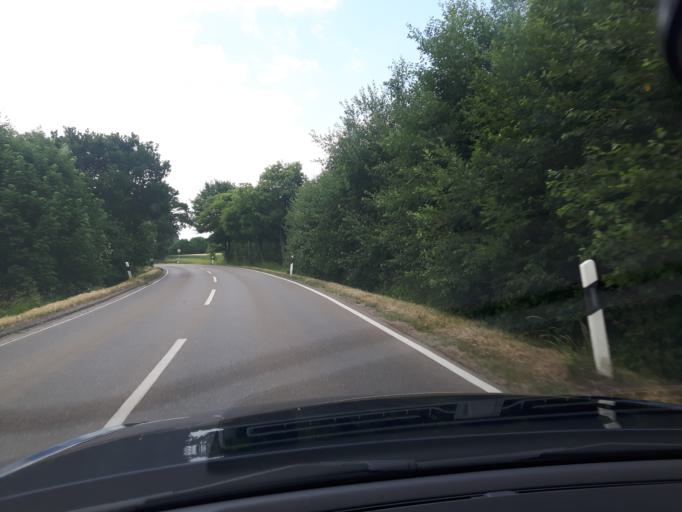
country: DE
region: Schleswig-Holstein
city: Sierksdorf
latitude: 54.0916
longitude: 10.7811
